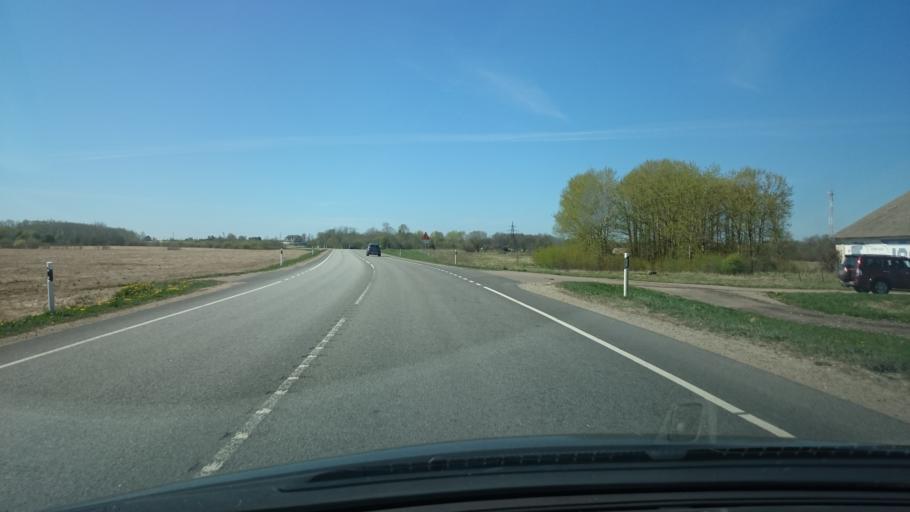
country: EE
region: Ida-Virumaa
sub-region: Narva-Joesuu linn
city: Narva-Joesuu
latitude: 59.3990
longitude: 28.0733
